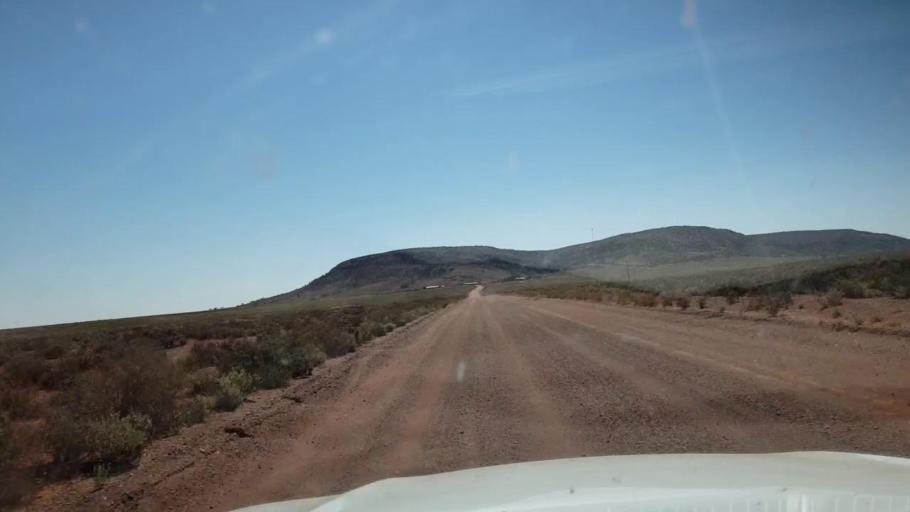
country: AU
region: South Australia
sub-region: Whyalla
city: Whyalla
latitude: -32.6970
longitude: 137.1322
